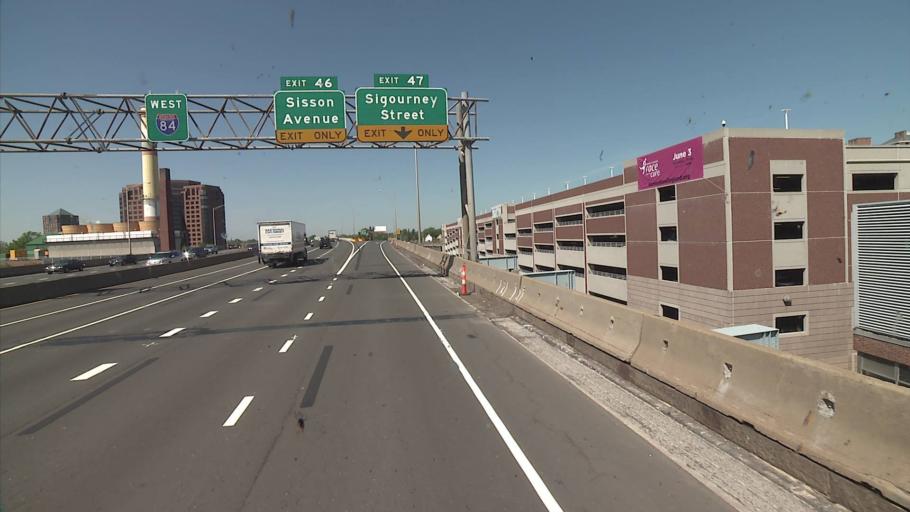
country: US
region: Connecticut
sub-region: Hartford County
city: Hartford
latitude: 41.7654
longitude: -72.6906
